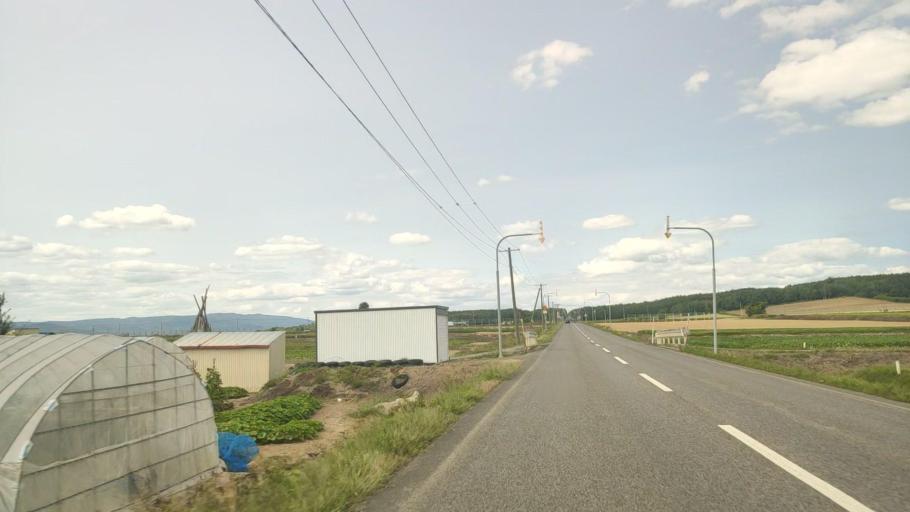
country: JP
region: Hokkaido
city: Nayoro
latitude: 44.2324
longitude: 142.4157
